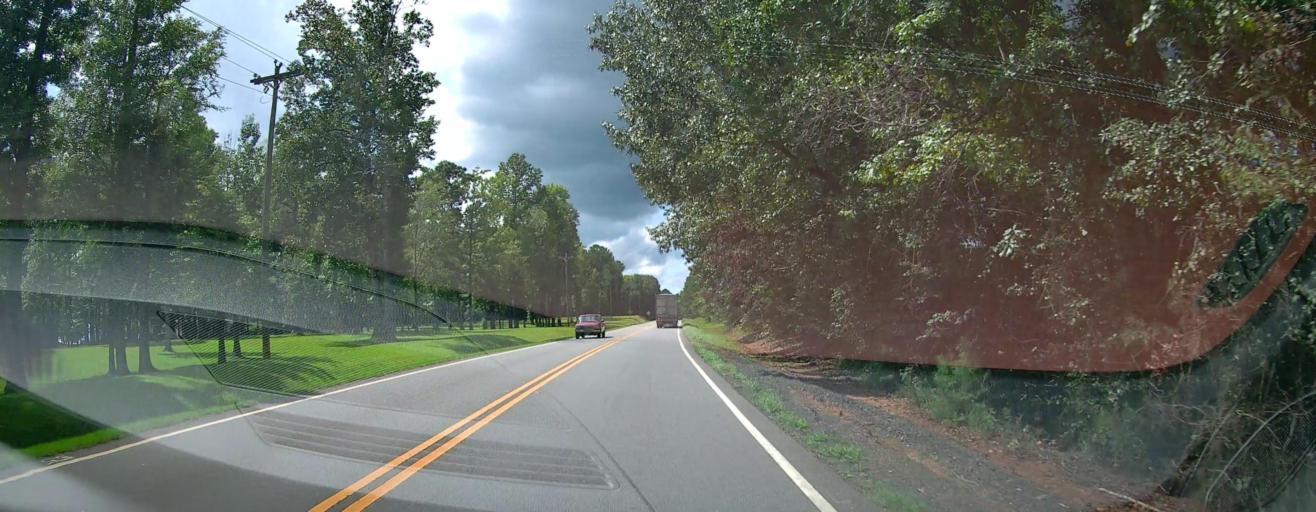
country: US
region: Georgia
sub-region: Bibb County
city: West Point
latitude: 32.8650
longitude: -83.8969
